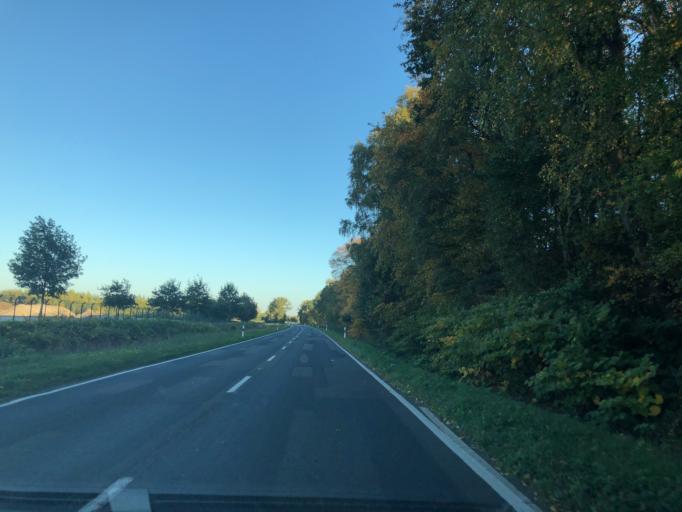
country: DE
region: Lower Saxony
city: Friesoythe
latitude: 53.0292
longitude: 7.7761
